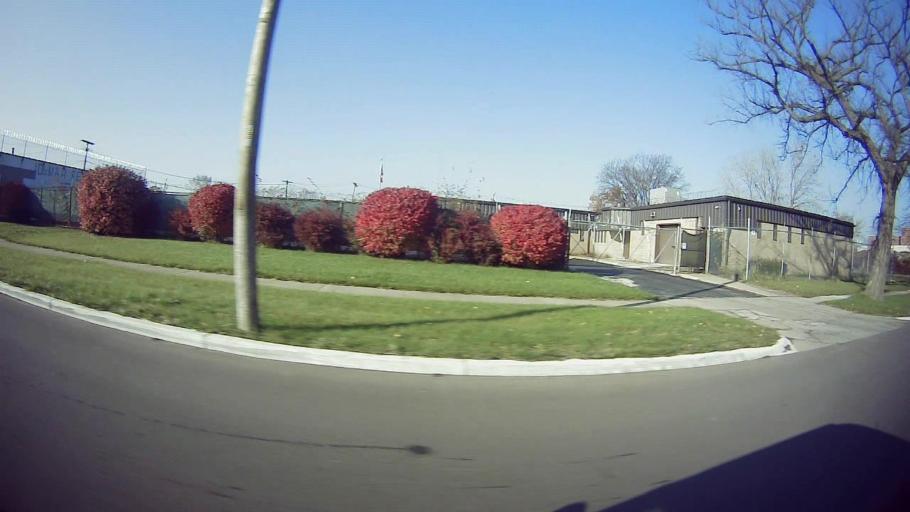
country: US
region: Michigan
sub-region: Wayne County
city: Dearborn
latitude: 42.3707
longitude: -83.1518
